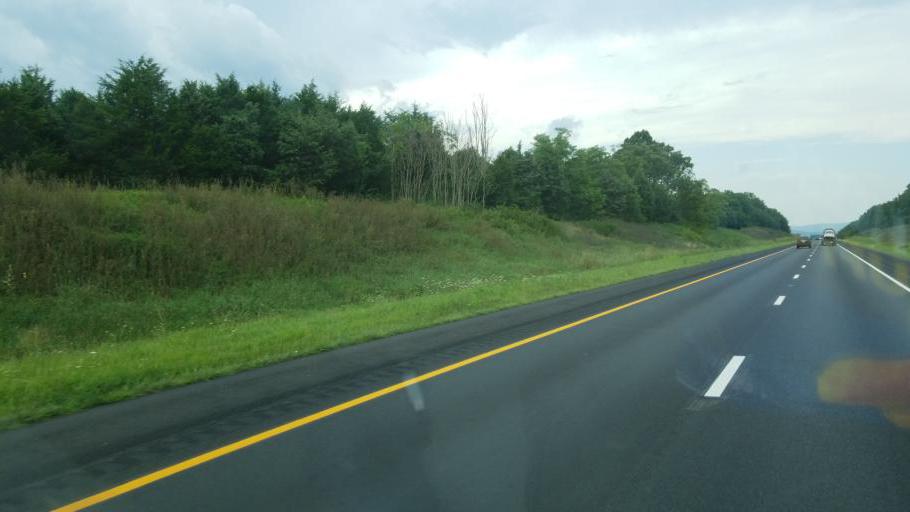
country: US
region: Virginia
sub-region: Frederick County
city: Middletown
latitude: 38.9815
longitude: -78.2280
